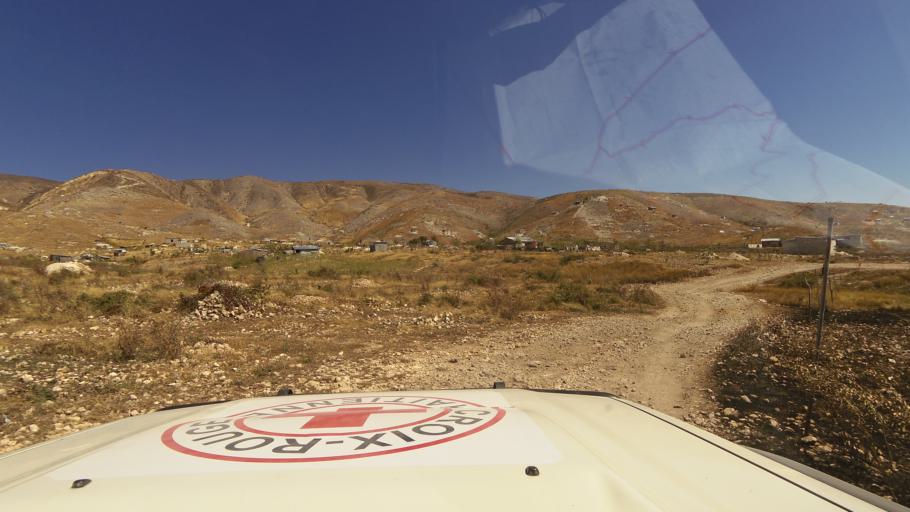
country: HT
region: Ouest
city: Croix des Bouquets
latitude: 18.6742
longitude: -72.2879
